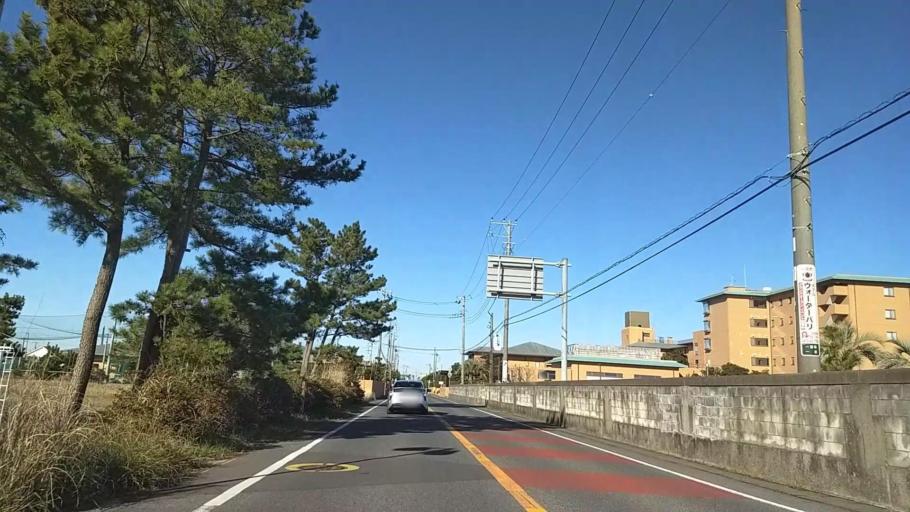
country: JP
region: Chiba
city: Mobara
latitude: 35.3738
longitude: 140.3876
